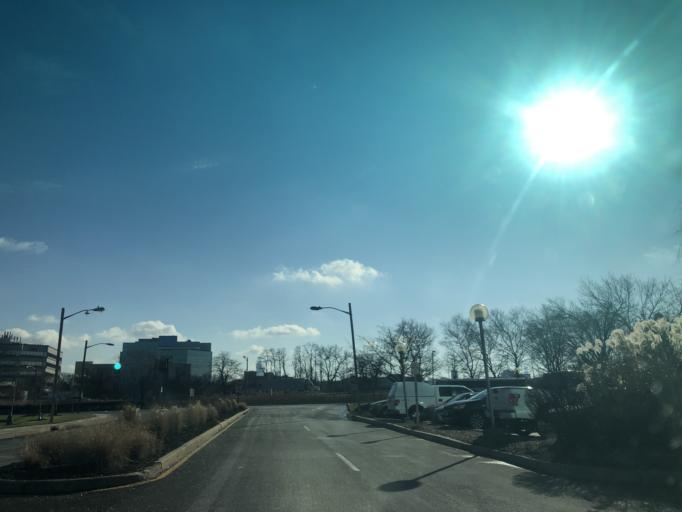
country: US
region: New Jersey
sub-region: Hudson County
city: Secaucus
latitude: 40.7905
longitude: -74.0494
